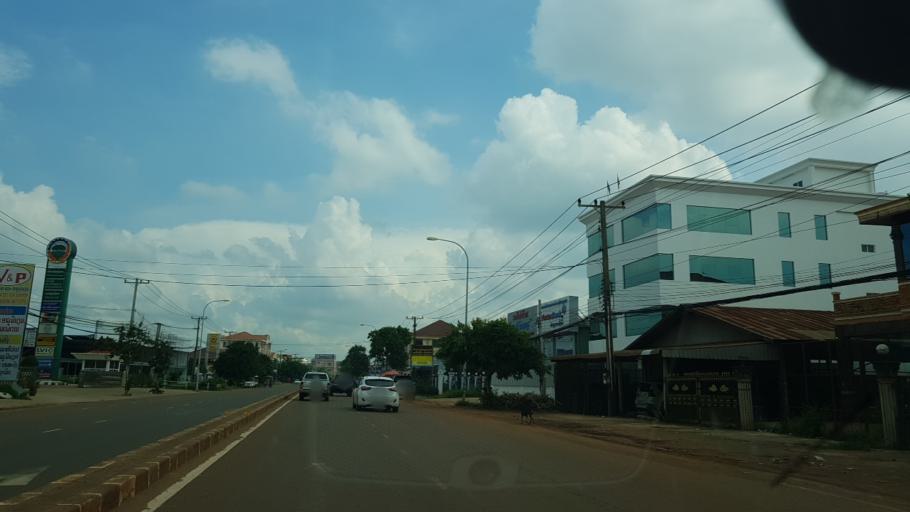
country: LA
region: Vientiane
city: Vientiane
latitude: 18.0255
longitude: 102.6516
